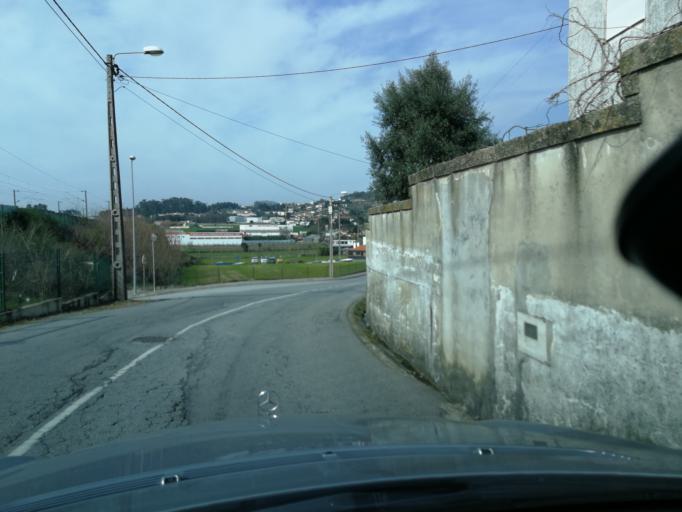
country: PT
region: Braga
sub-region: Vila Nova de Famalicao
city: Vila Nova de Famalicao
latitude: 41.4307
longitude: -8.5225
